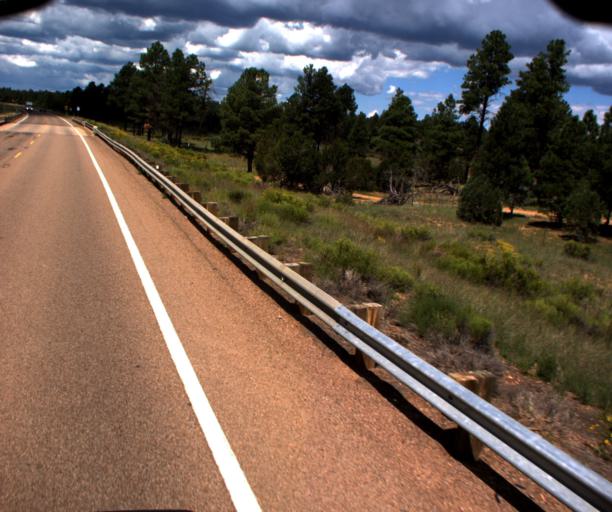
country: US
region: Arizona
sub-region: Navajo County
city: Heber-Overgaard
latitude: 34.3934
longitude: -110.5162
